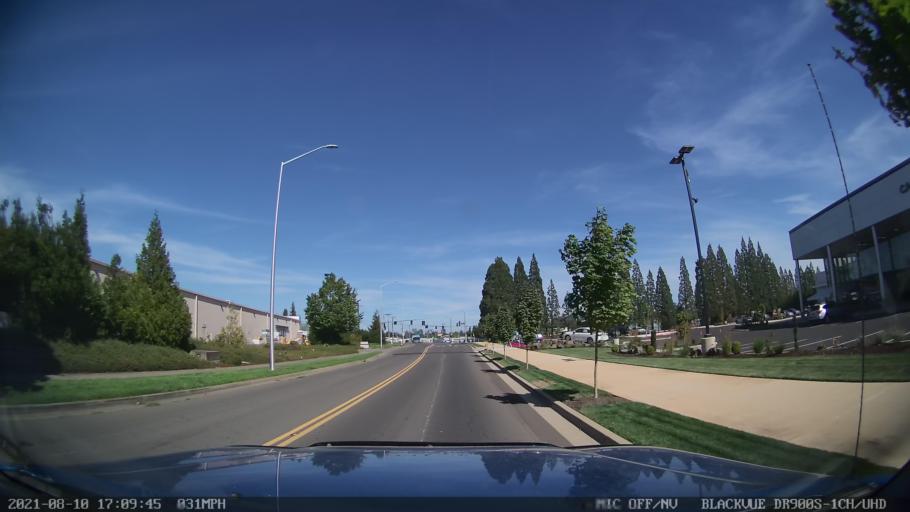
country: US
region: Oregon
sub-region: Marion County
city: Keizer
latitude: 44.9695
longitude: -123.0220
